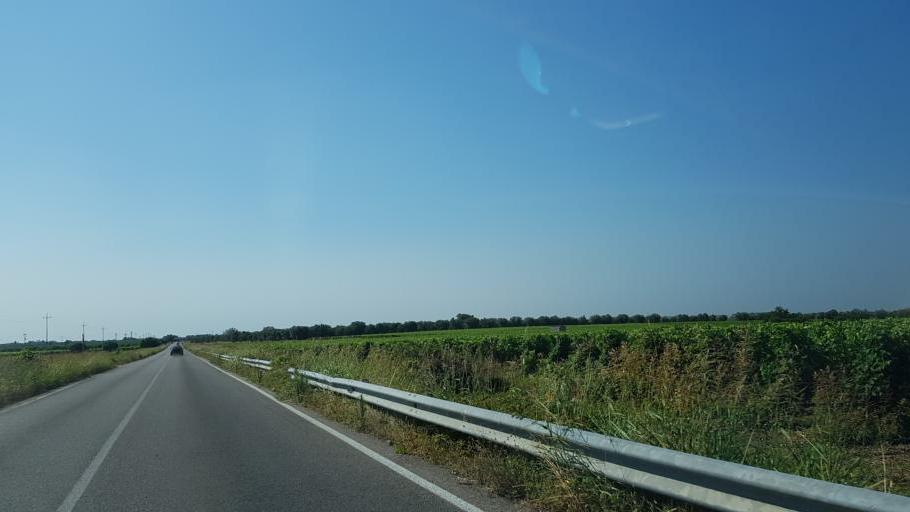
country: IT
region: Apulia
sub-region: Provincia di Lecce
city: Guagnano
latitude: 40.4283
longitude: 17.9431
